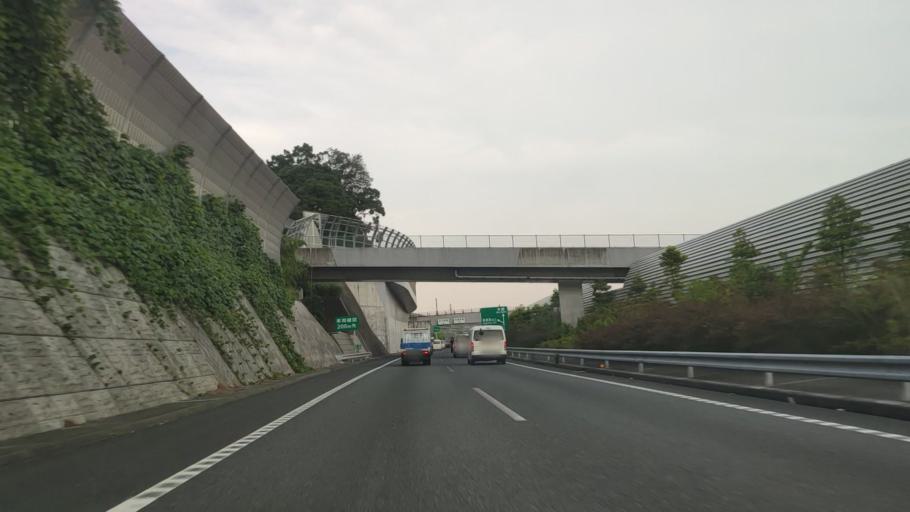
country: JP
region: Tokyo
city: Hachioji
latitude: 35.5951
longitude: 139.2825
